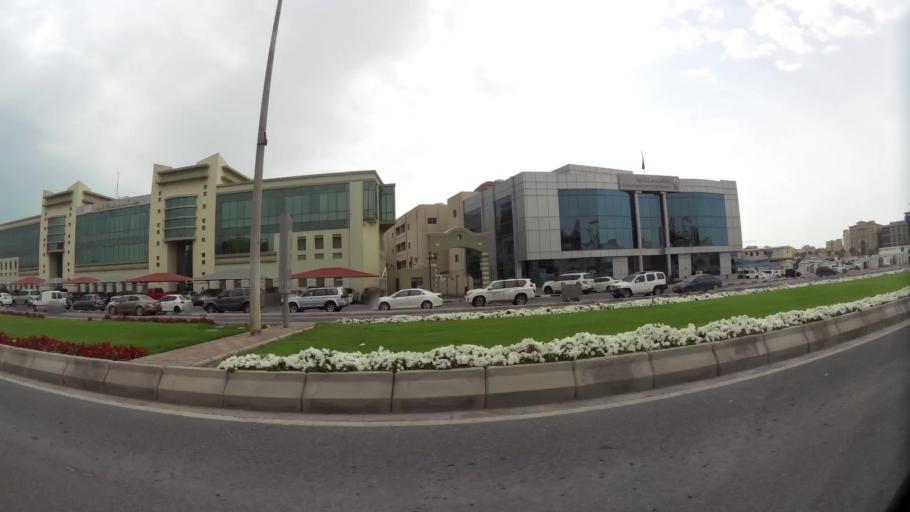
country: QA
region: Baladiyat ad Dawhah
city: Doha
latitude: 25.2959
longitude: 51.4980
